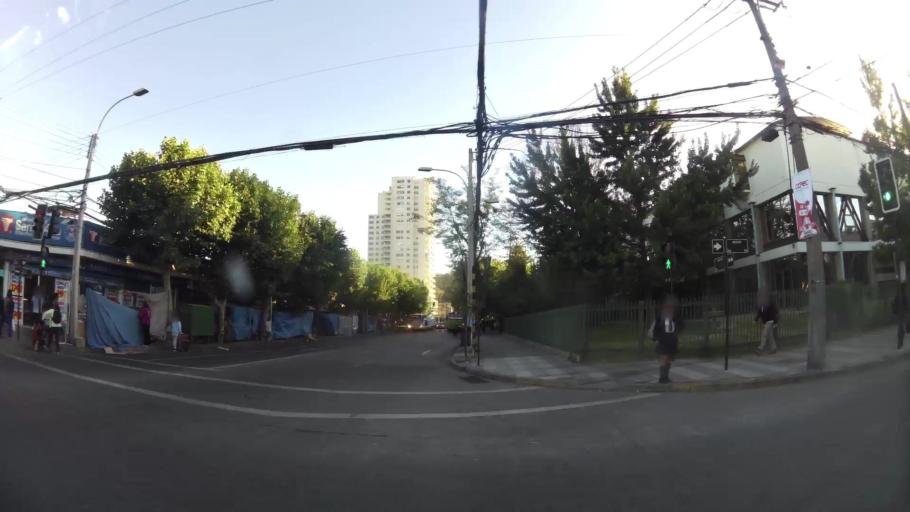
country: CL
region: Valparaiso
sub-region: Provincia de Valparaiso
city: Vina del Mar
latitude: -33.0244
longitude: -71.5491
